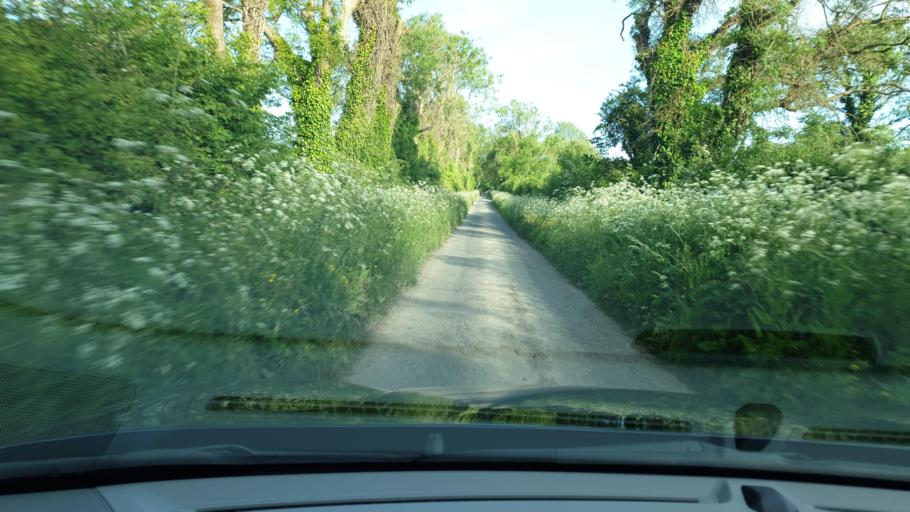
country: IE
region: Leinster
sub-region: An Mhi
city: Ashbourne
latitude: 53.5552
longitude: -6.4286
